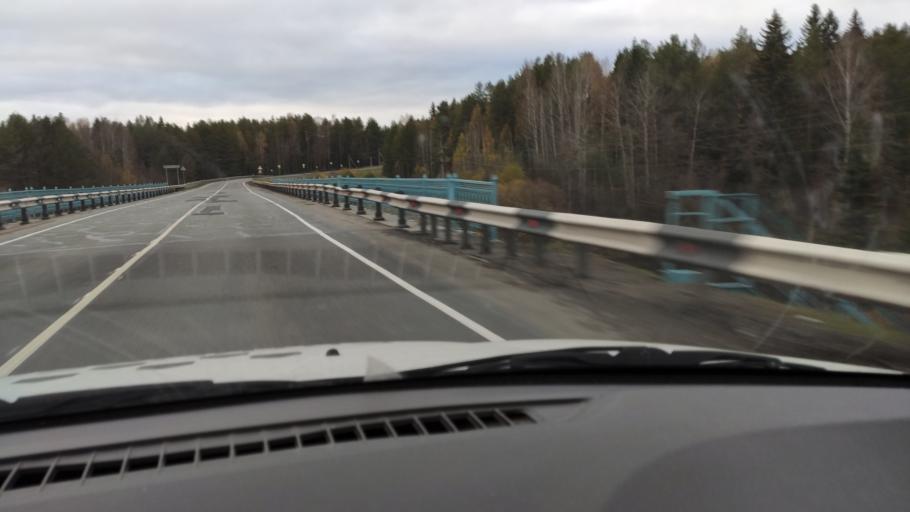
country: RU
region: Kirov
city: Belaya Kholunitsa
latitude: 58.8360
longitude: 50.6889
